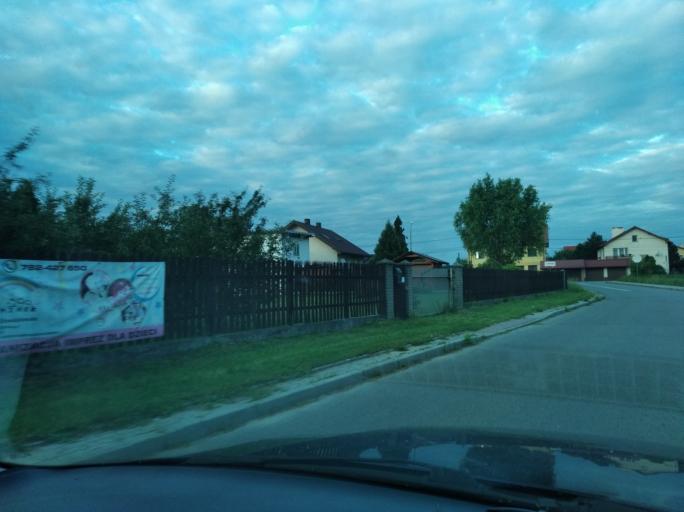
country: PL
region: Subcarpathian Voivodeship
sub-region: Powiat ropczycko-sedziszowski
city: Sedziszow Malopolski
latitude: 50.0778
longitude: 21.6974
